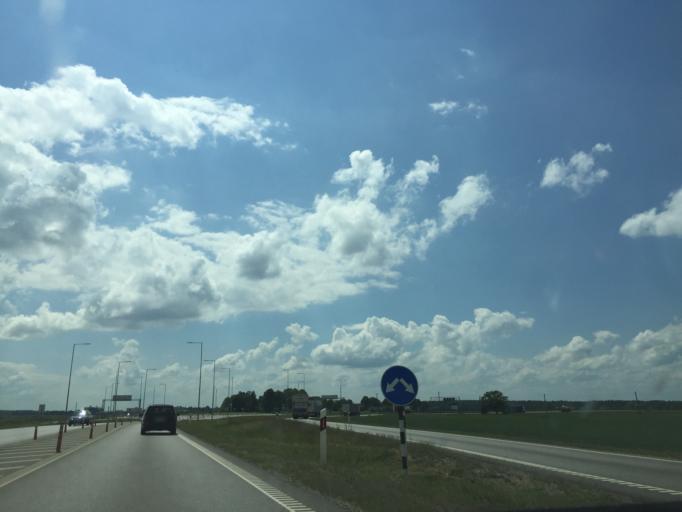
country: LT
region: Panevezys
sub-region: Panevezys City
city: Panevezys
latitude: 55.8054
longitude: 24.3684
